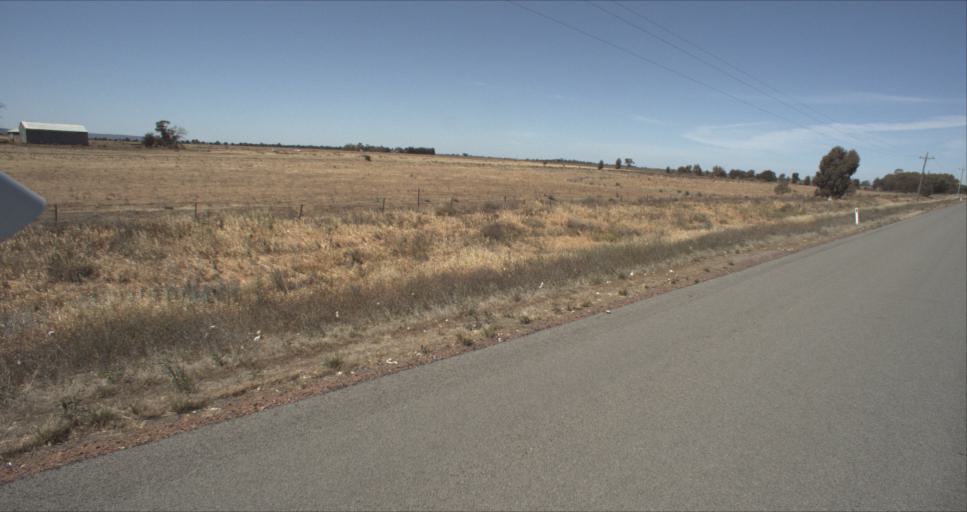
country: AU
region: New South Wales
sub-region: Leeton
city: Leeton
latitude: -34.4319
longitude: 146.2995
